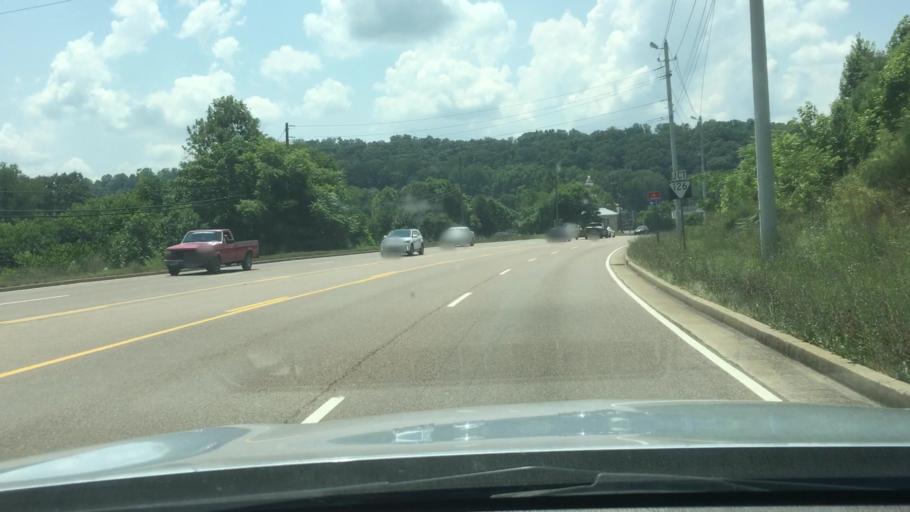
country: US
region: Tennessee
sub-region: Sullivan County
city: Blountville
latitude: 36.5364
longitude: -82.3280
